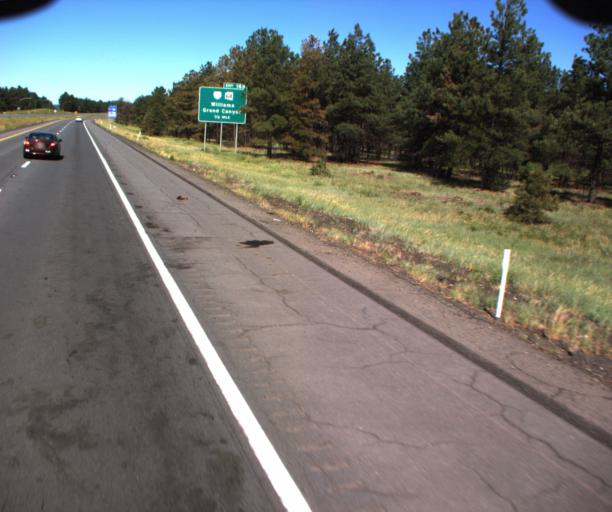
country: US
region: Arizona
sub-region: Coconino County
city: Williams
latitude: 35.2582
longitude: -112.1376
